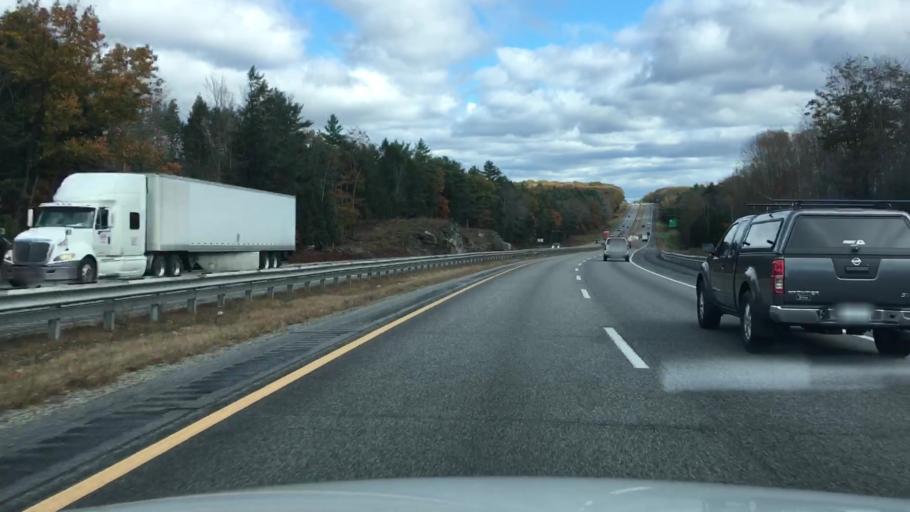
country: US
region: Maine
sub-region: Cumberland County
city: Freeport
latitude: 43.9019
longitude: -70.0719
